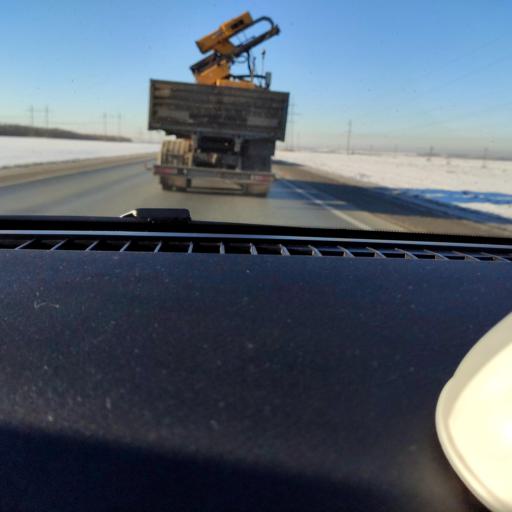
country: RU
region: Samara
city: Smyshlyayevka
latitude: 53.1465
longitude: 50.4767
